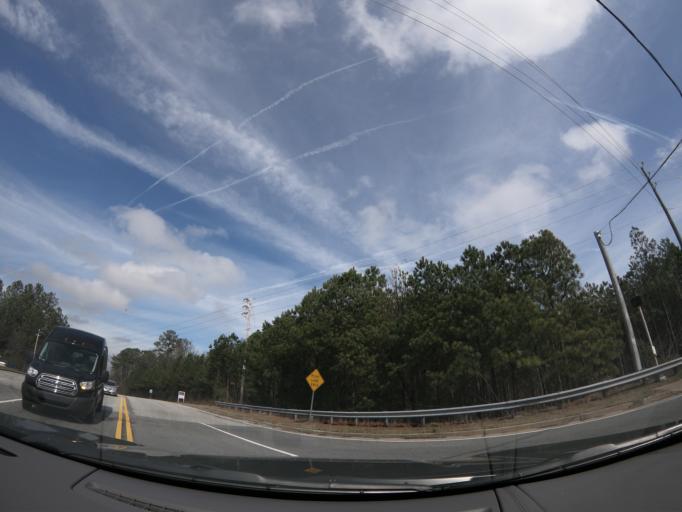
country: US
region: Georgia
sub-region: Fulton County
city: College Park
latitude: 33.6347
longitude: -84.4680
